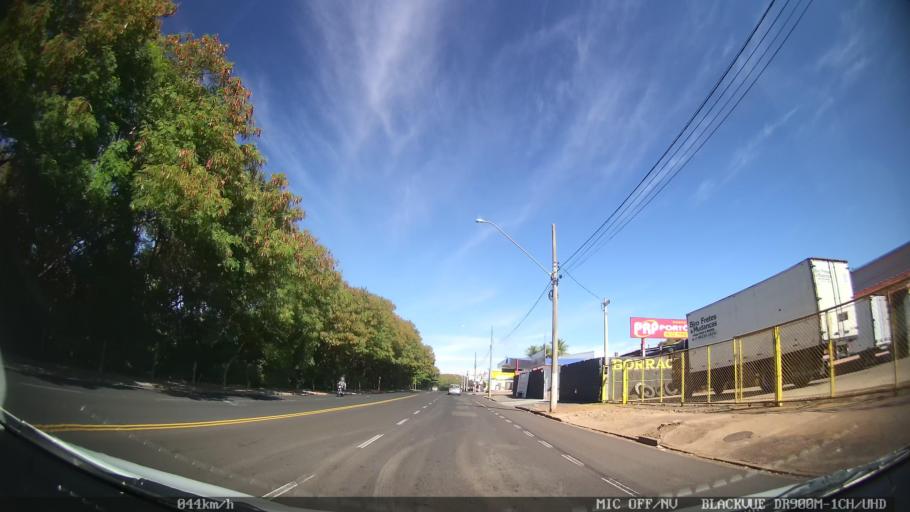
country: BR
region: Sao Paulo
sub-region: Sao Jose Do Rio Preto
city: Sao Jose do Rio Preto
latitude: -20.7991
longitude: -49.4025
